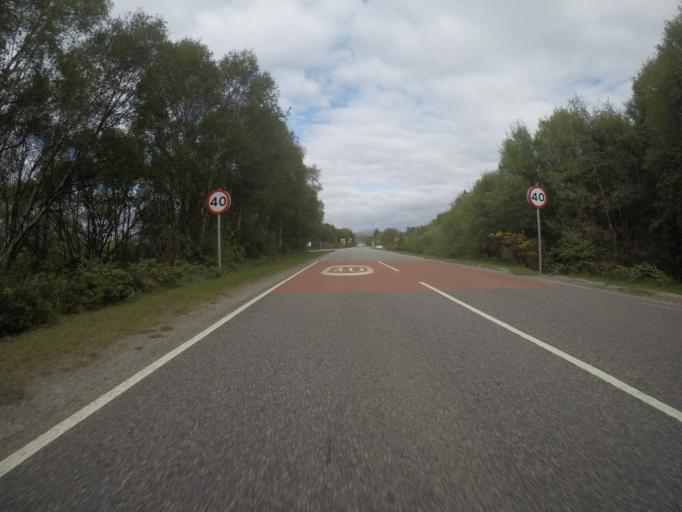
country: GB
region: Scotland
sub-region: Highland
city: Portree
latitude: 57.2715
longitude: -5.7496
